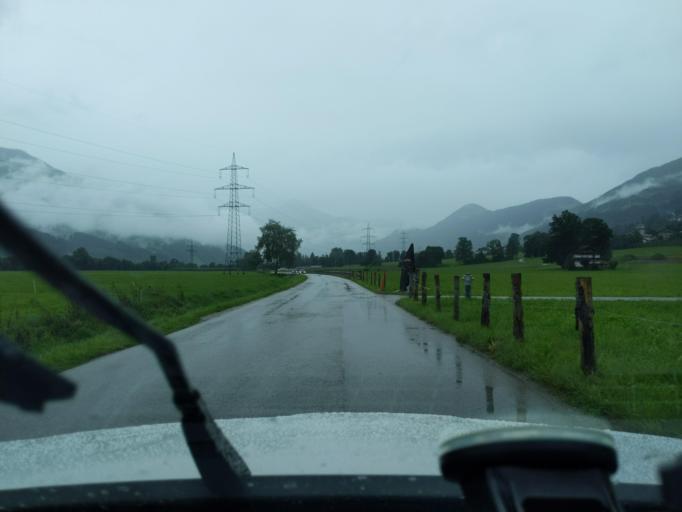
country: AT
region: Tyrol
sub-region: Politischer Bezirk Schwaz
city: Hart im Zillertal
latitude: 47.3382
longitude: 11.8678
